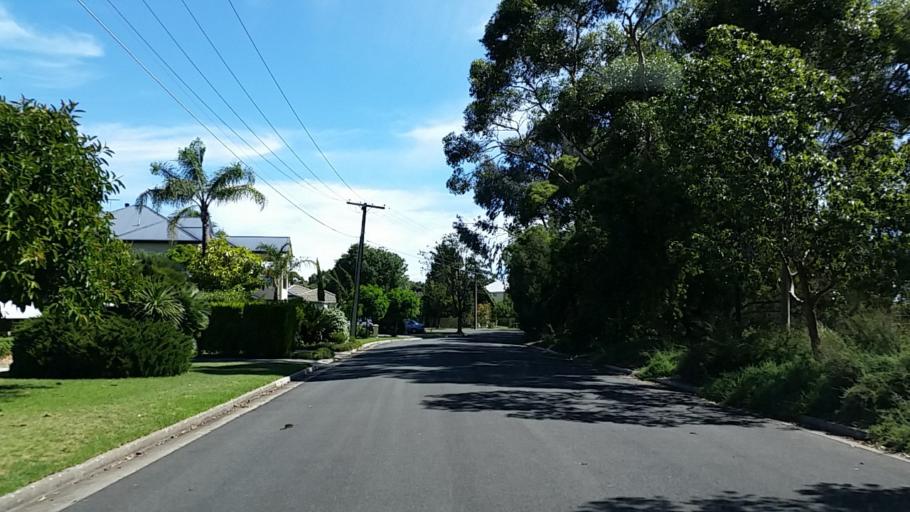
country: AU
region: South Australia
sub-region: Charles Sturt
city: Seaton
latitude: -34.9197
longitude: 138.5224
